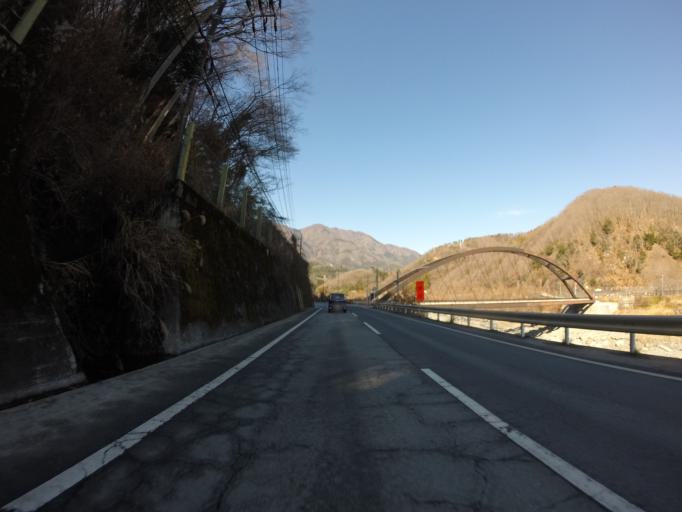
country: JP
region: Yamanashi
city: Ryuo
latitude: 35.4324
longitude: 138.4224
